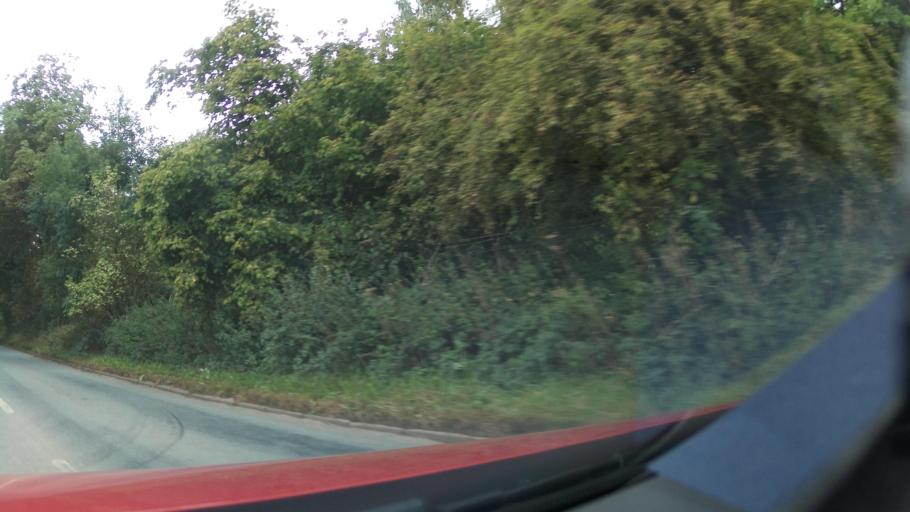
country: GB
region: England
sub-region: Staffordshire
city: Eccleshall
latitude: 52.8979
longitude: -2.2148
